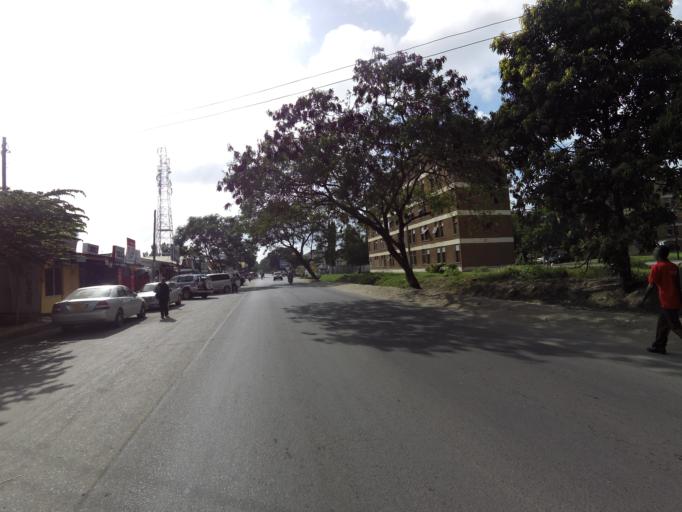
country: TZ
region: Dar es Salaam
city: Magomeni
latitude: -6.7697
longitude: 39.2296
